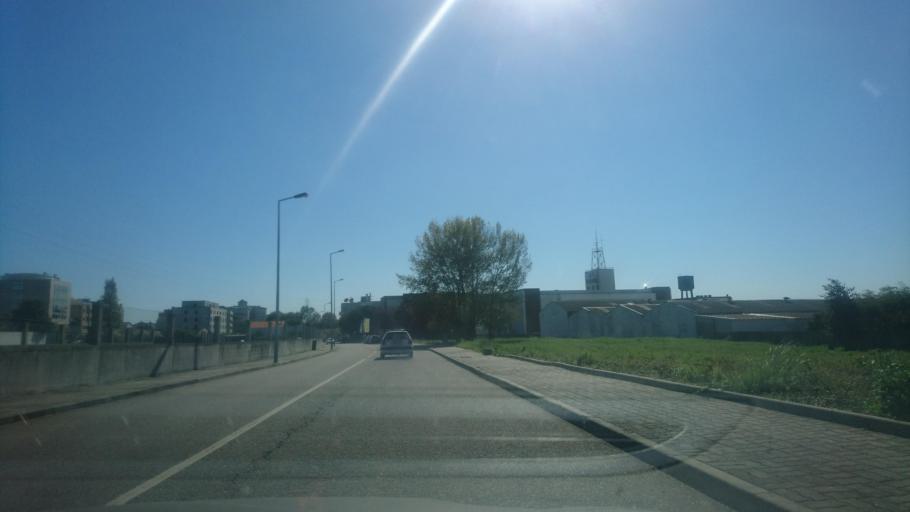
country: PT
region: Aveiro
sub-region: Ovar
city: Esmoriz
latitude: 40.9597
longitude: -8.6321
